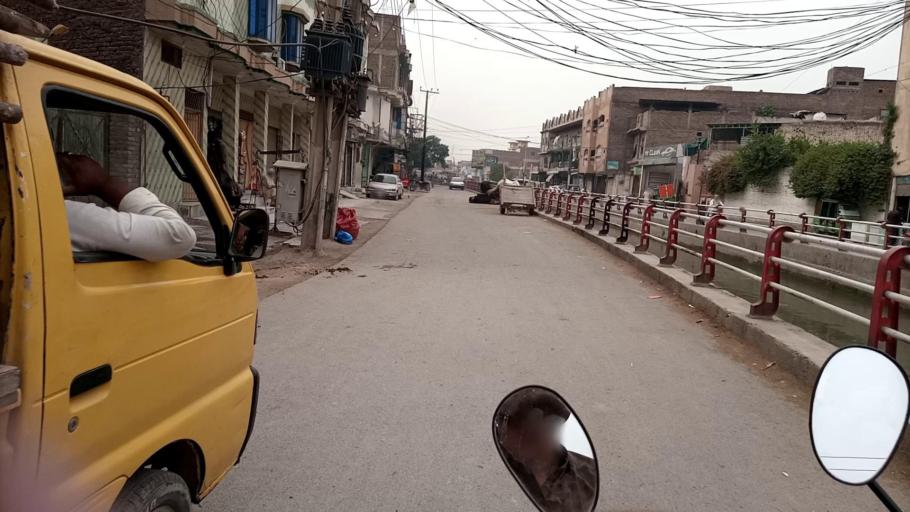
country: PK
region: Khyber Pakhtunkhwa
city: Peshawar
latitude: 34.0214
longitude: 71.5923
